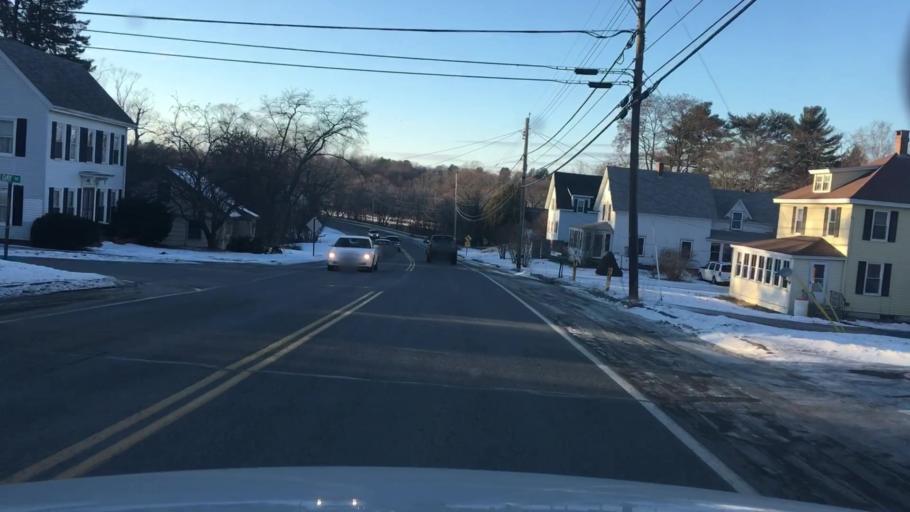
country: US
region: Maine
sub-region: Penobscot County
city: Eddington
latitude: 44.8188
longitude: -68.7109
